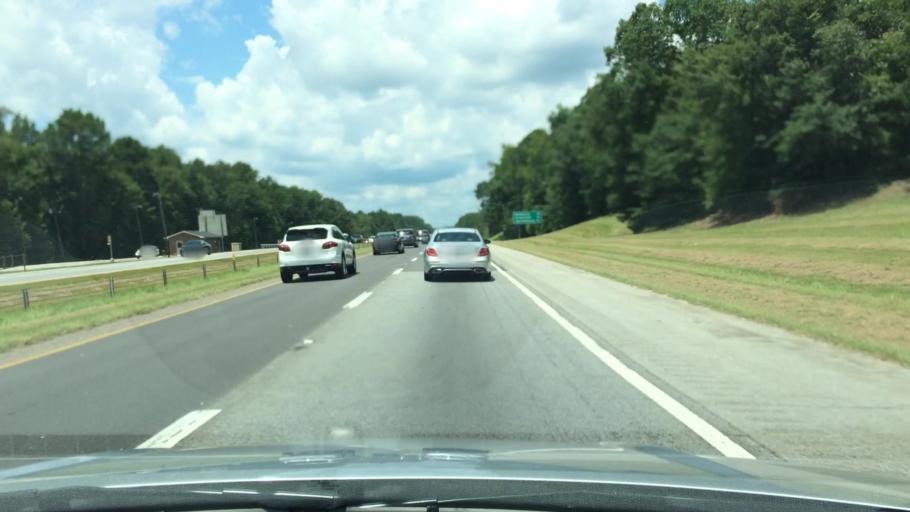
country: US
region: South Carolina
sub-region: Newberry County
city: Prosperity
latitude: 34.2451
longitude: -81.4751
